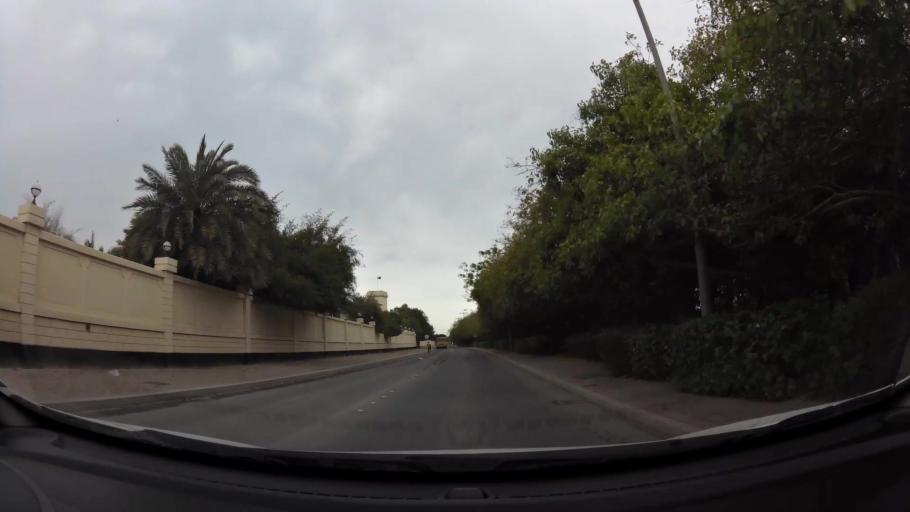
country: BH
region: Central Governorate
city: Madinat Hamad
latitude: 26.1560
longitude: 50.4528
